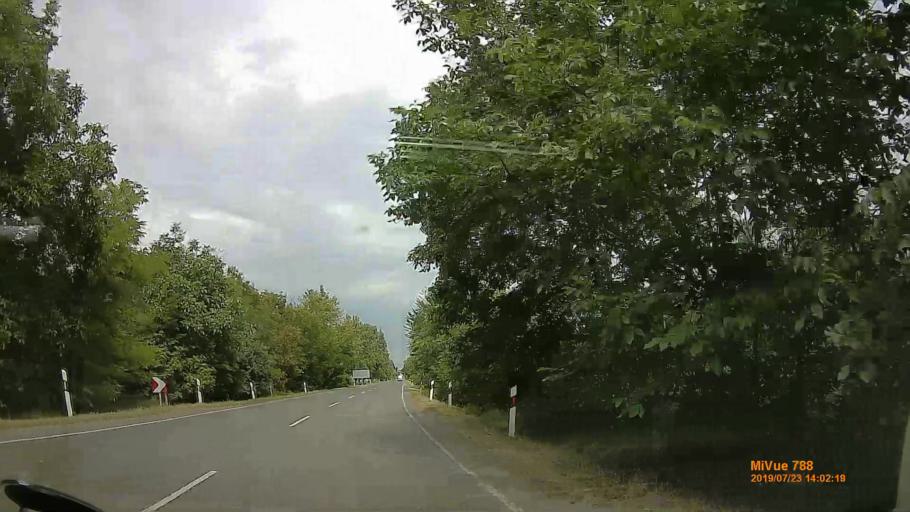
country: HU
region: Szabolcs-Szatmar-Bereg
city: Tiszavasvari
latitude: 47.9548
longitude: 21.3331
